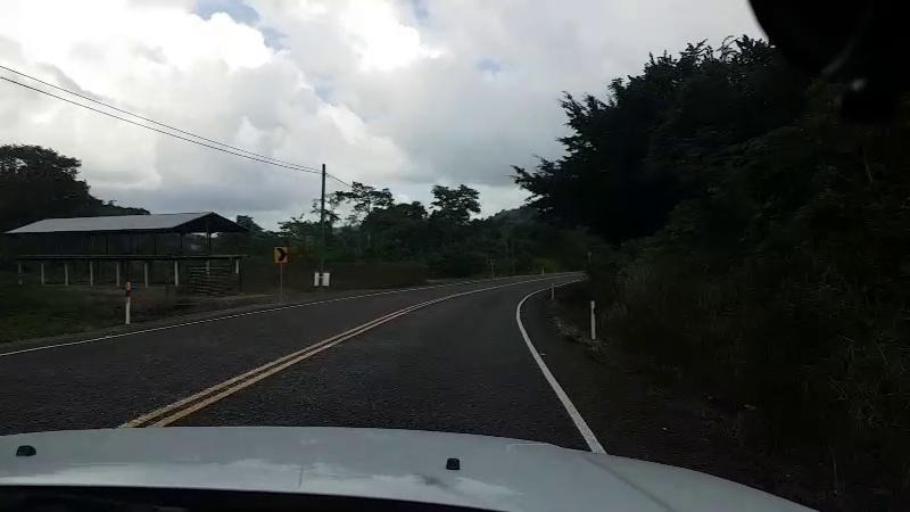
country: BZ
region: Cayo
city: Belmopan
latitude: 17.1496
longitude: -88.7122
